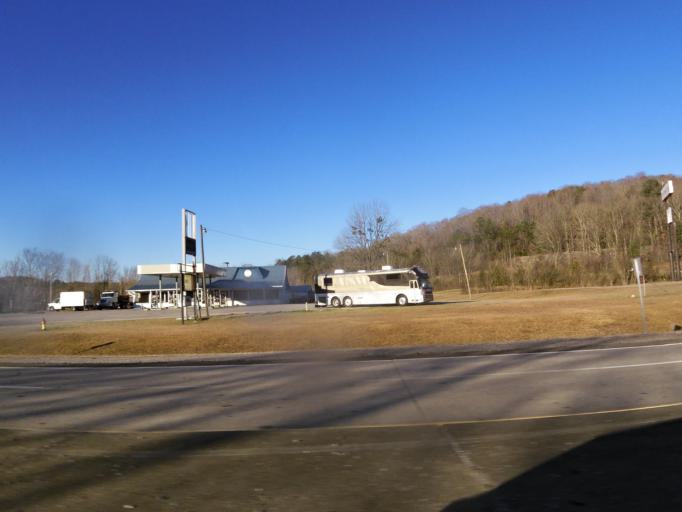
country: US
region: Alabama
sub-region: Morgan County
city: Falkville
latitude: 34.3129
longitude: -86.8995
